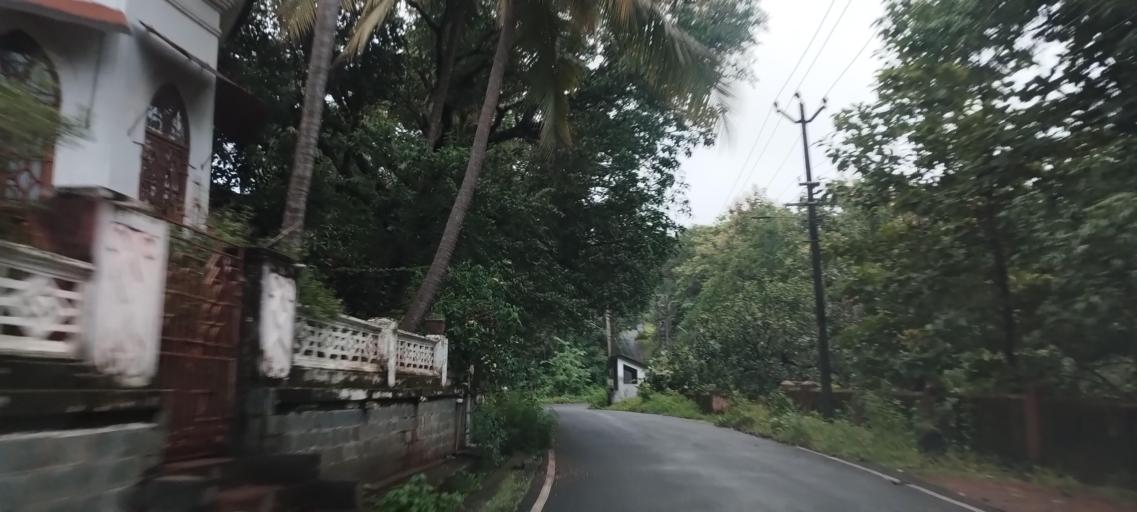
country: IN
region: Goa
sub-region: North Goa
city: Jua
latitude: 15.5224
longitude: 73.8986
